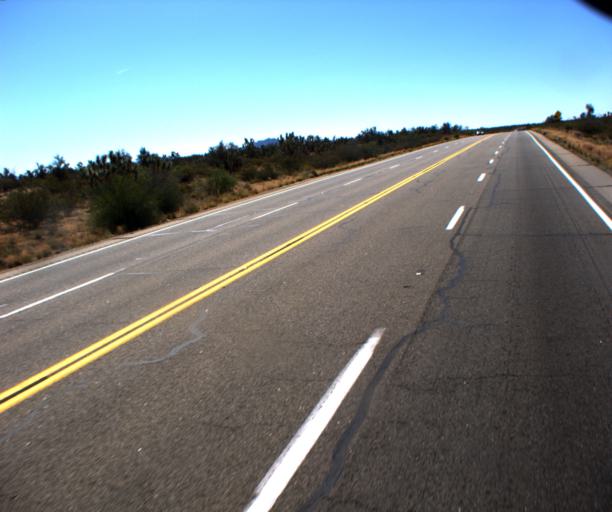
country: US
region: Arizona
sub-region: Yavapai County
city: Congress
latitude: 34.2790
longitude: -113.1012
